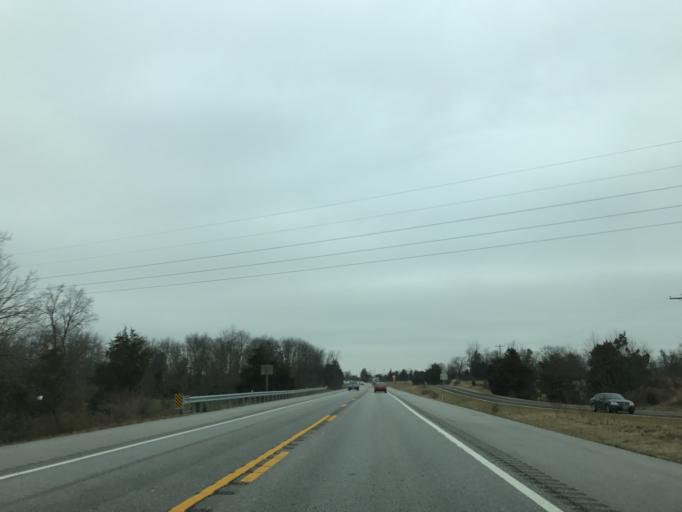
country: US
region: Maryland
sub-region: Carroll County
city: Taneytown
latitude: 39.6487
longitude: -77.1478
